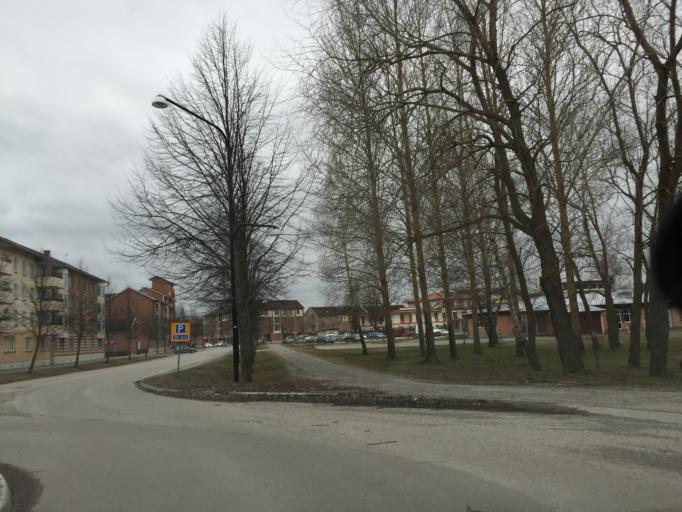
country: SE
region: OErebro
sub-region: Orebro Kommun
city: Orebro
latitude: 59.2588
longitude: 15.2107
